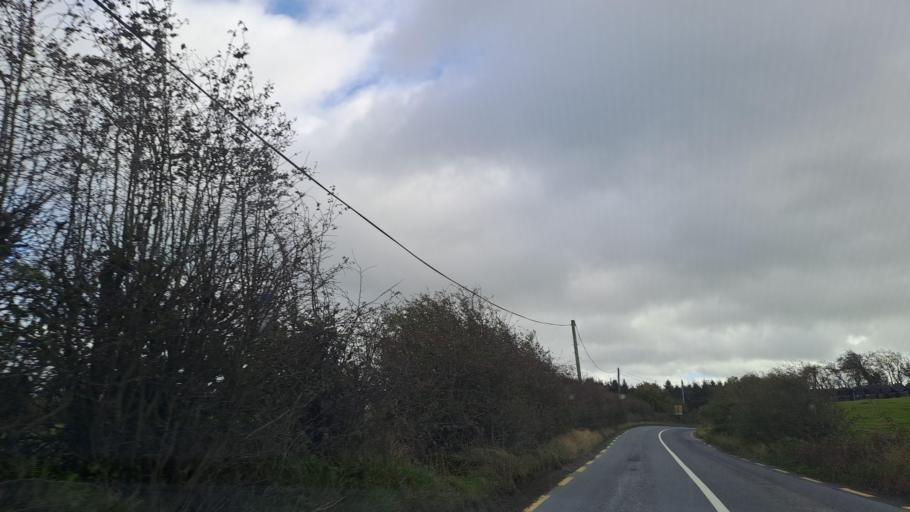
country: IE
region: Ulster
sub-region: An Cabhan
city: Kingscourt
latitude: 53.9304
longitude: -6.8827
